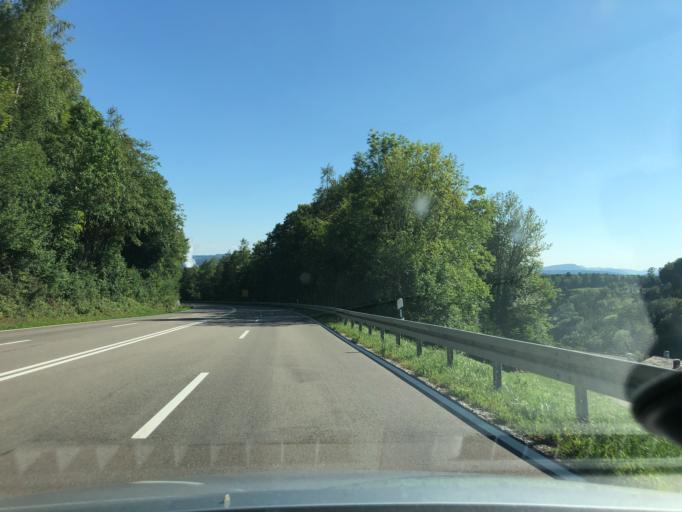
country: DE
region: Baden-Wuerttemberg
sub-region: Freiburg Region
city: Dogern
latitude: 47.6300
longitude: 8.1843
